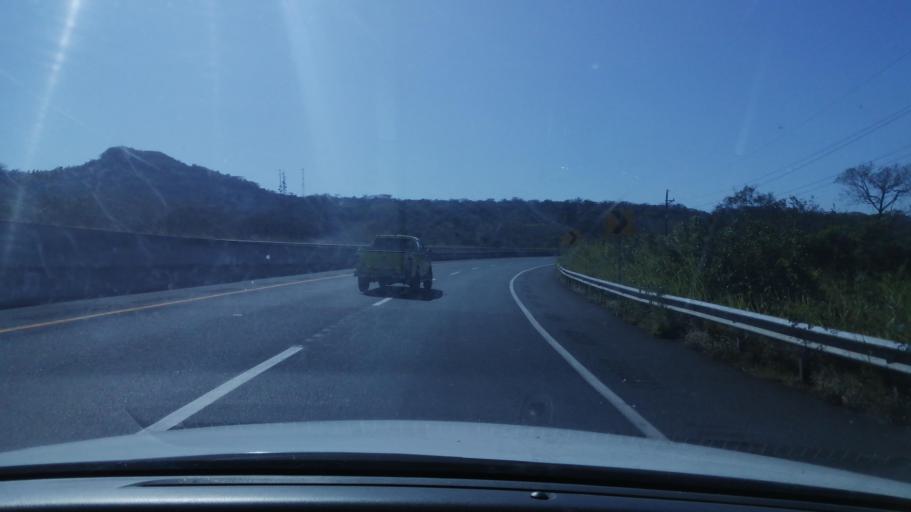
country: PA
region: Chiriqui
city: San Felix
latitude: 8.2783
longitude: -82.0543
